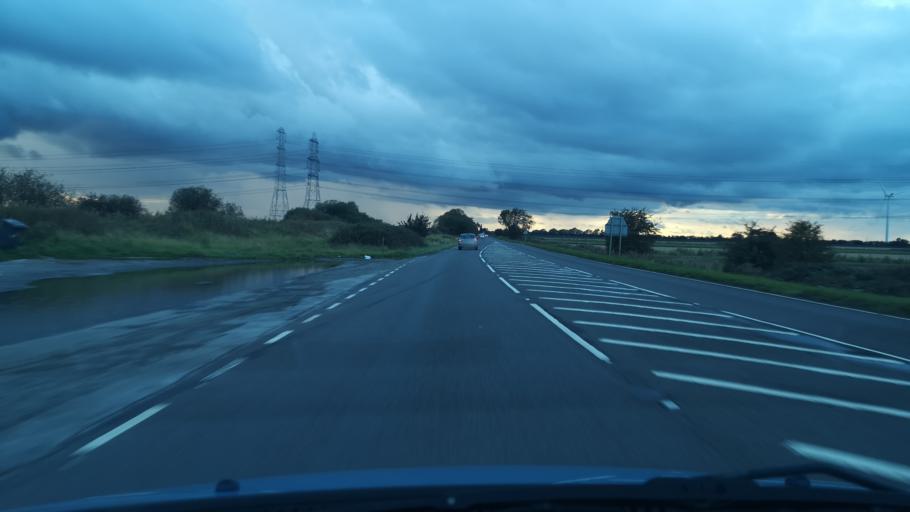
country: GB
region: England
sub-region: North Lincolnshire
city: Gunness
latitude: 53.5767
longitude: -0.7559
